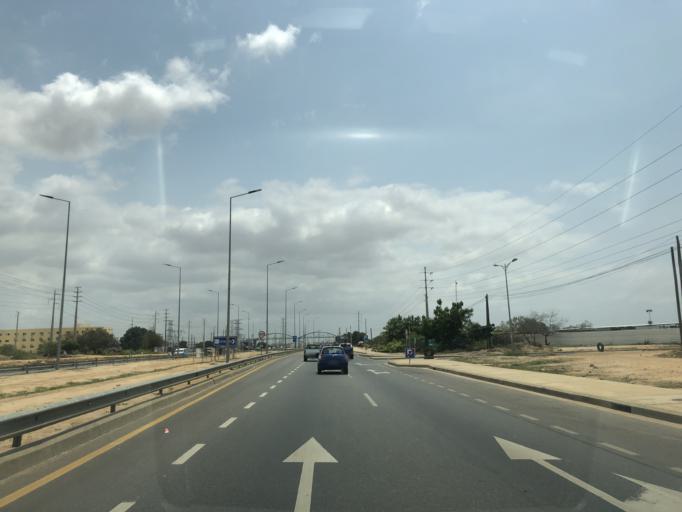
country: AO
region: Luanda
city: Luanda
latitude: -8.9637
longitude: 13.2561
